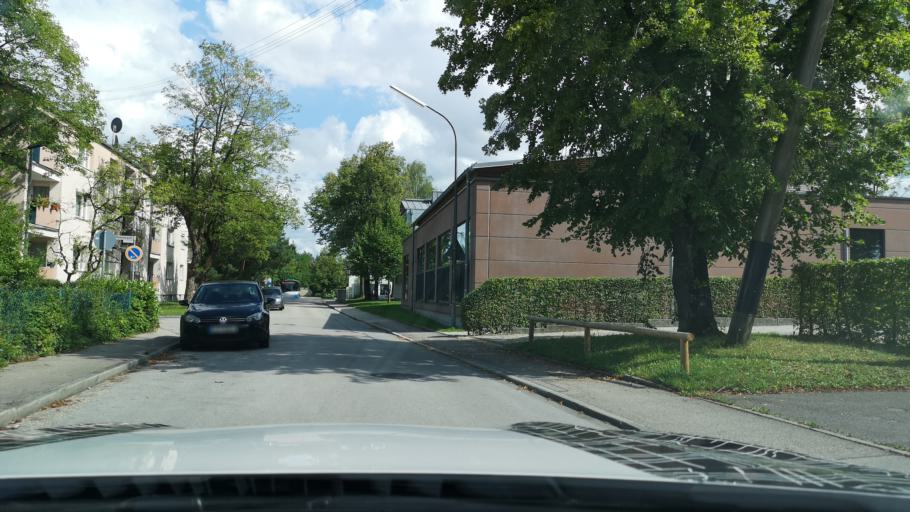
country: DE
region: Bavaria
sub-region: Upper Bavaria
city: Oberschleissheim
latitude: 48.2479
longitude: 11.6067
